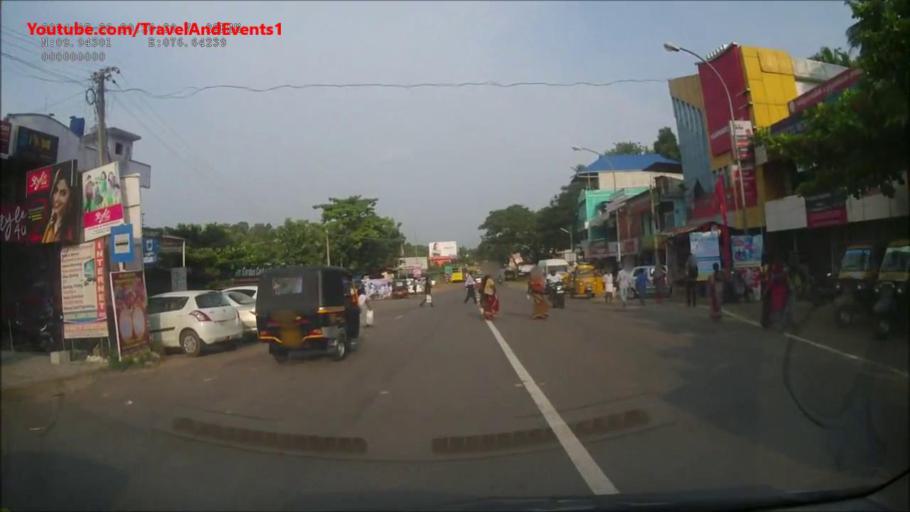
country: IN
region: Kerala
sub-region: Ernakulam
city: Muvattupula
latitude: 9.9386
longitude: 76.6508
